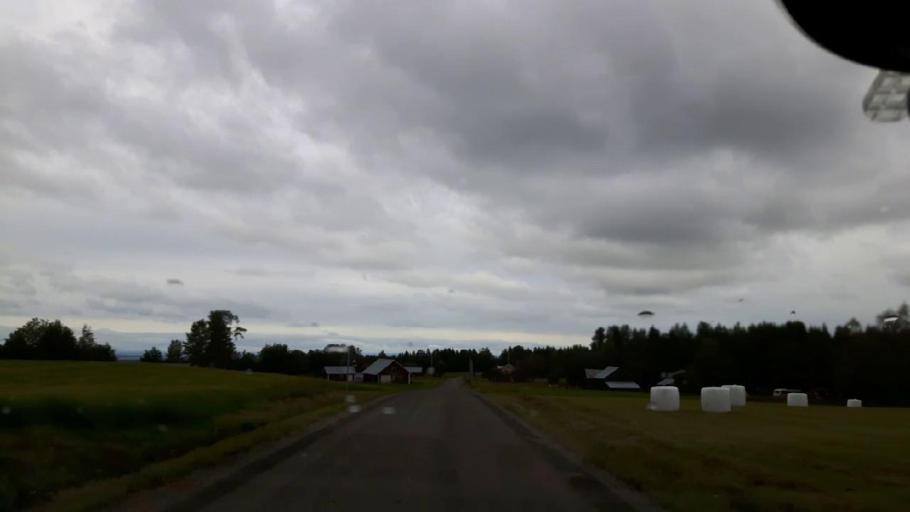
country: SE
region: Jaemtland
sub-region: OEstersunds Kommun
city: Ostersund
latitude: 63.0552
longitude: 14.5619
